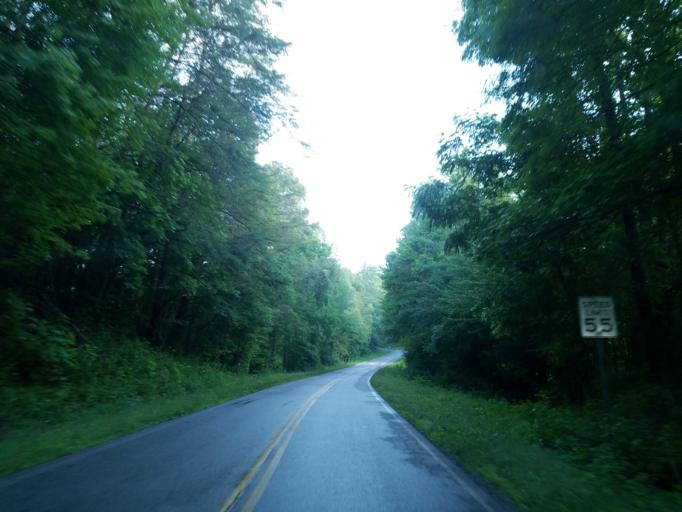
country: US
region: Georgia
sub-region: Fannin County
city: Blue Ridge
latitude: 34.7542
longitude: -84.2247
